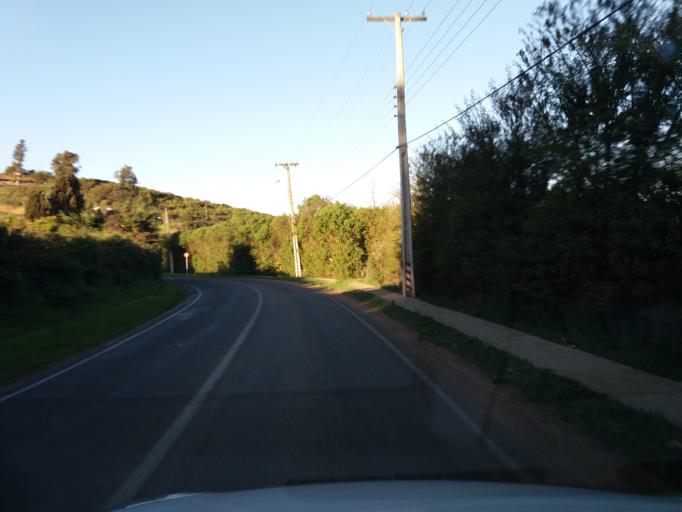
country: CL
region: Valparaiso
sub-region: Provincia de Quillota
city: Quillota
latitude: -32.8936
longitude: -71.2863
